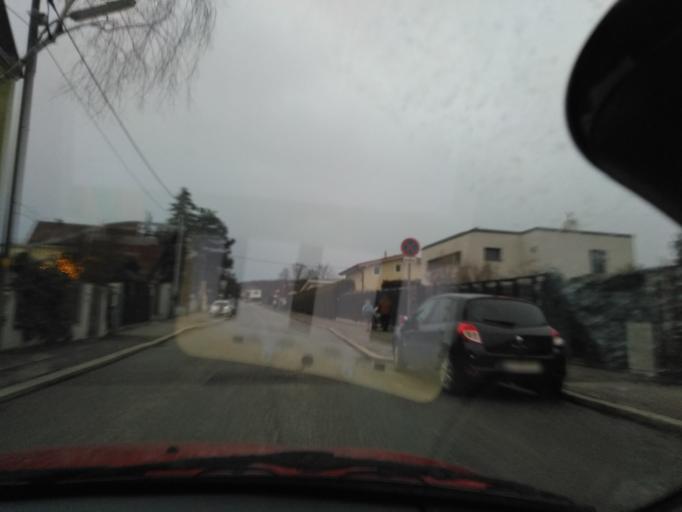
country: AT
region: Vienna
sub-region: Wien Stadt
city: Vienna
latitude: 48.2338
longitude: 16.3041
